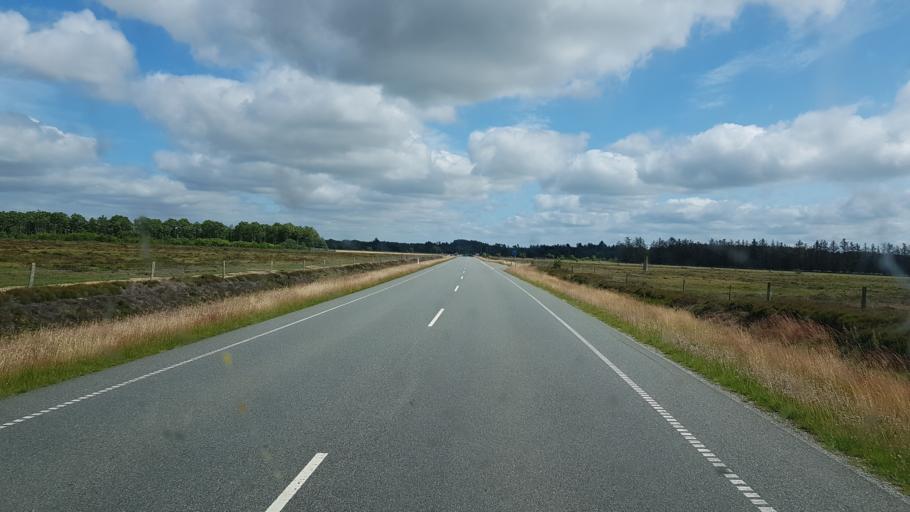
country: DK
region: South Denmark
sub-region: Billund Kommune
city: Grindsted
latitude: 55.7465
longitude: 8.9061
